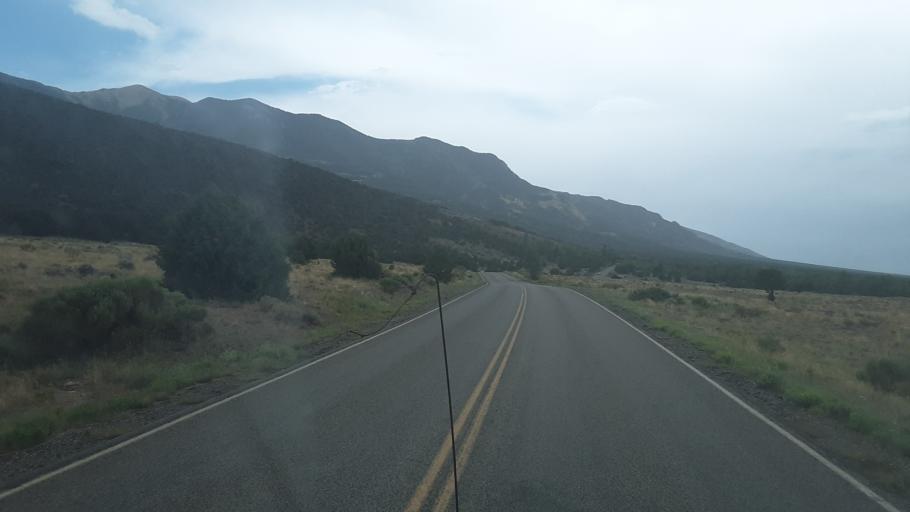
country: US
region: Colorado
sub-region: Custer County
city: Westcliffe
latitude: 37.7420
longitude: -105.5071
